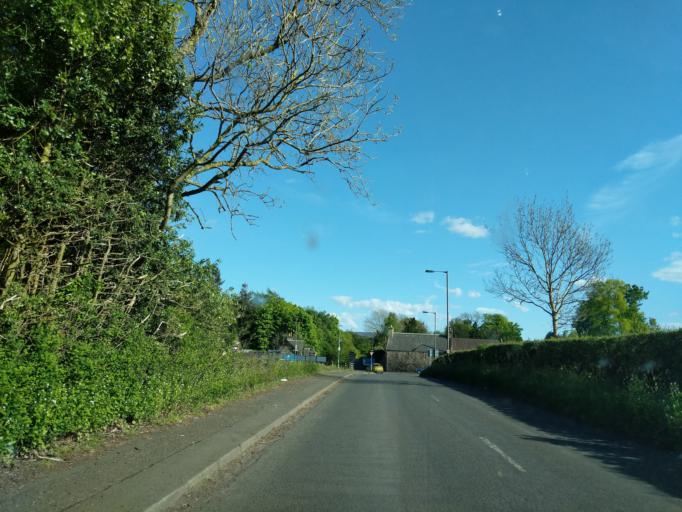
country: GB
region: Scotland
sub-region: Edinburgh
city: Ratho
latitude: 55.9088
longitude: -3.3694
